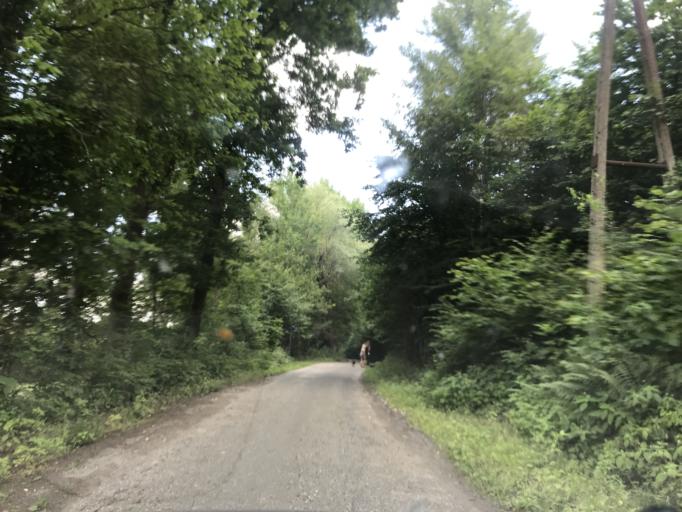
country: PL
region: West Pomeranian Voivodeship
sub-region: Powiat stargardzki
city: Insko
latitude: 53.4797
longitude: 15.5102
